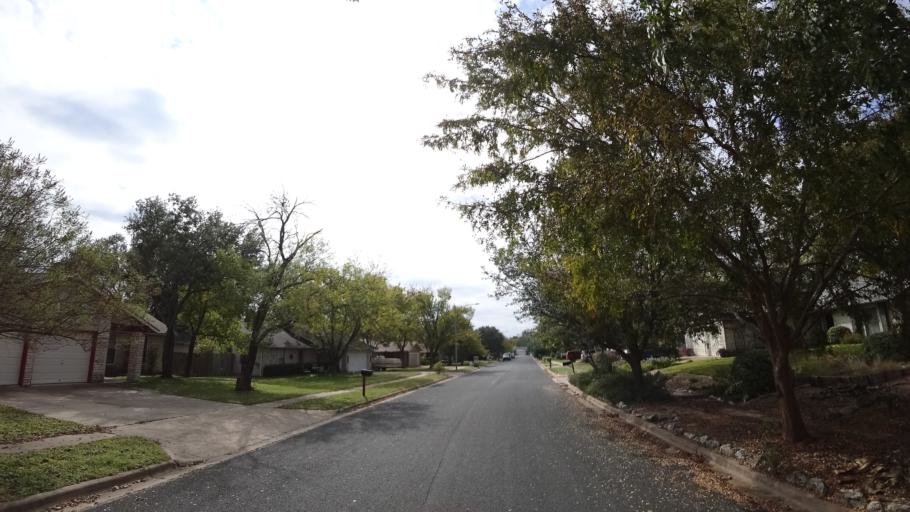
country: US
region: Texas
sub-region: Travis County
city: Wells Branch
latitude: 30.4224
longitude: -97.6938
